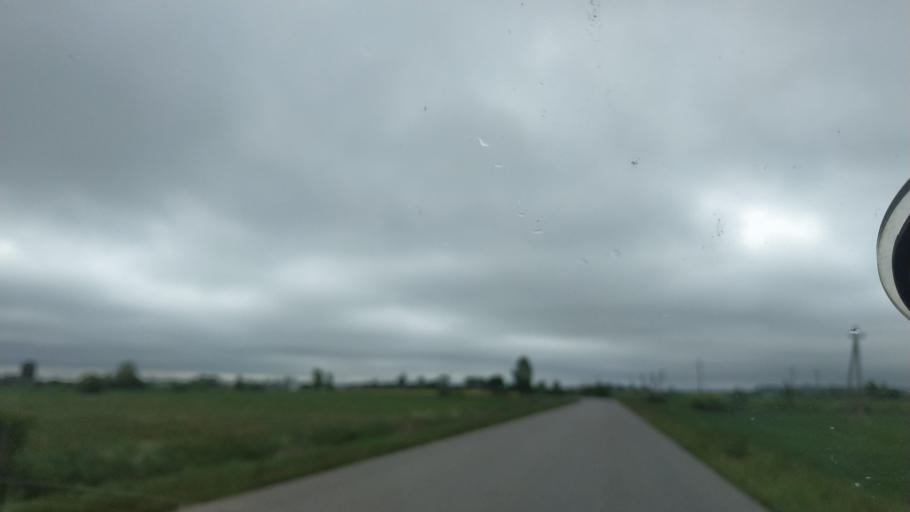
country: LT
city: Vabalninkas
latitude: 55.9726
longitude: 24.7444
